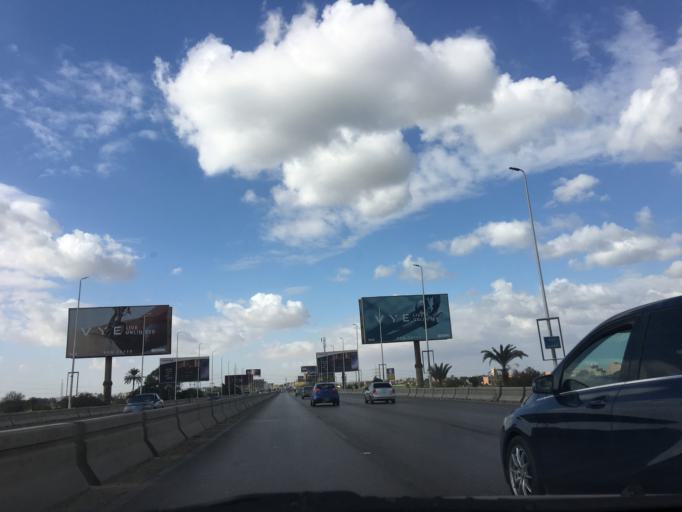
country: EG
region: Al Jizah
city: Awsim
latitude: 30.0645
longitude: 31.1607
